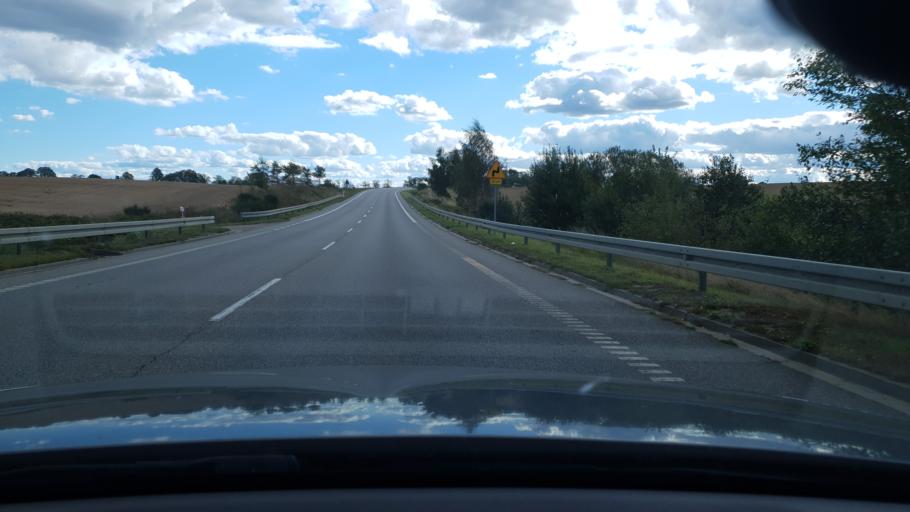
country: PL
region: Pomeranian Voivodeship
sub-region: Powiat pucki
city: Zelistrzewo
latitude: 54.6778
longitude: 18.3743
